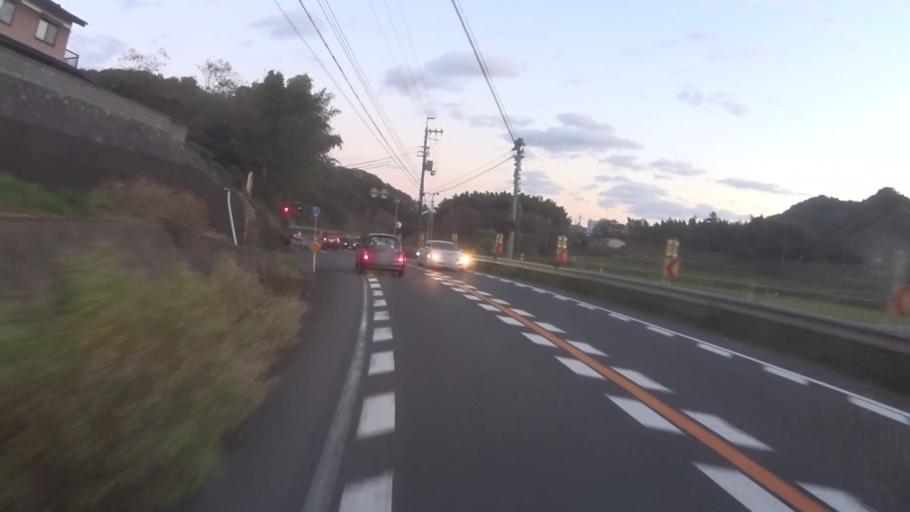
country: JP
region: Kyoto
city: Ayabe
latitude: 35.1906
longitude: 135.3626
